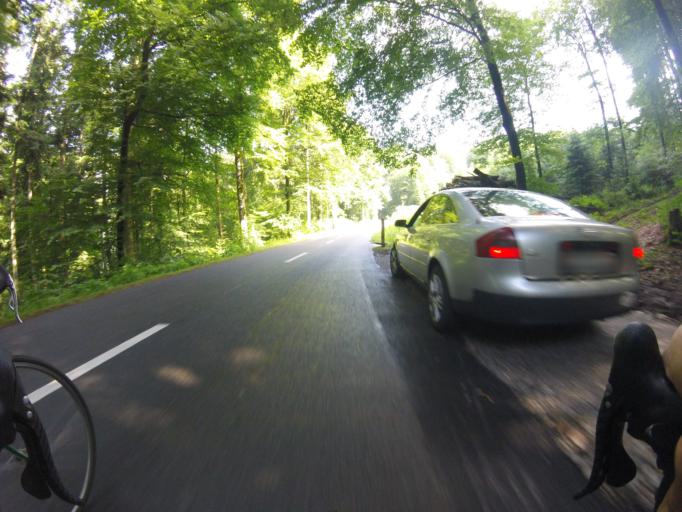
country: CH
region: Bern
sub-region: Bern-Mittelland District
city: Worb
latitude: 46.9369
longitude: 7.5720
